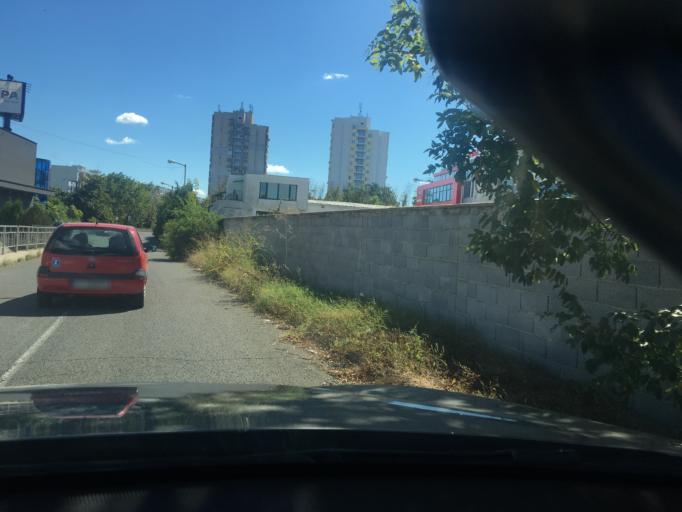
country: BG
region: Burgas
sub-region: Obshtina Burgas
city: Burgas
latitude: 42.5301
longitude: 27.4557
